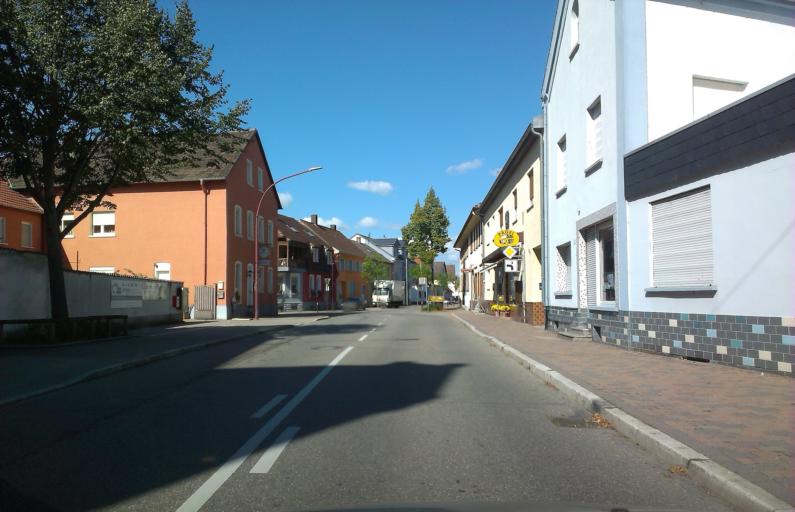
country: DE
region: Rheinland-Pfalz
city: Germersheim
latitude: 49.2326
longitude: 8.4097
